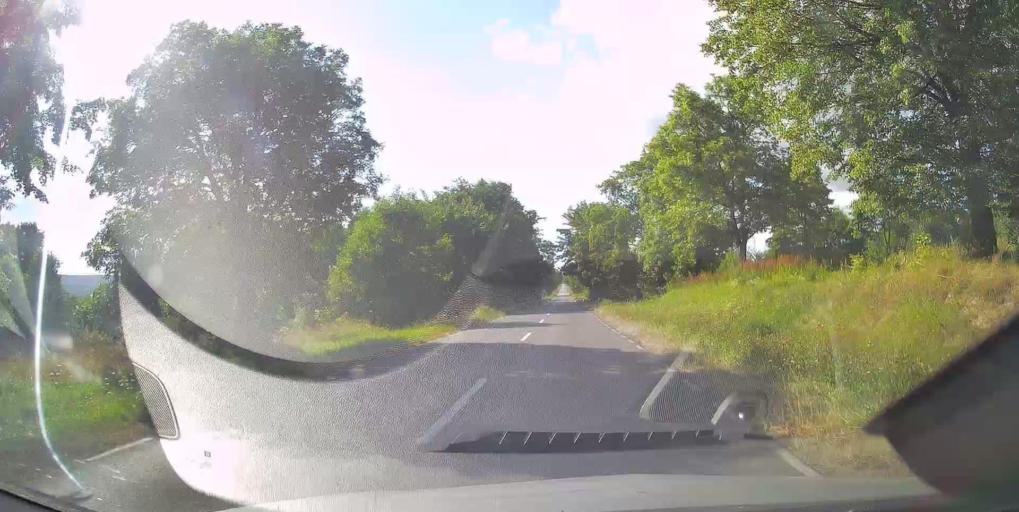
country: PL
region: Swietokrzyskie
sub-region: Powiat kielecki
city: Bodzentyn
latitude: 50.9594
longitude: 20.9073
